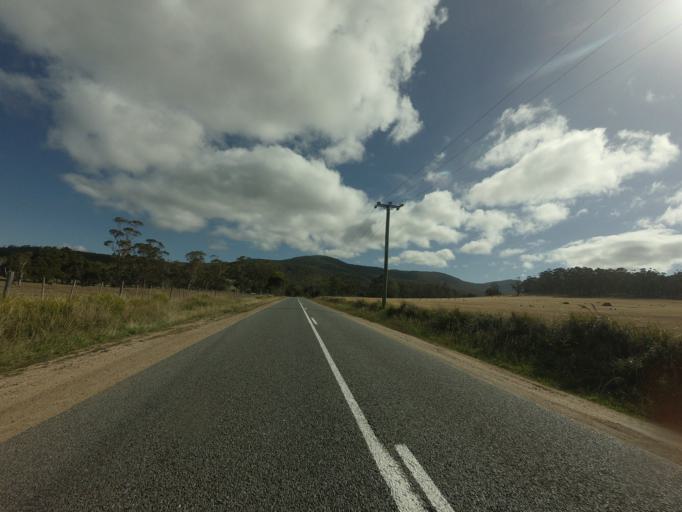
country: AU
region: Tasmania
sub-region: Break O'Day
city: St Helens
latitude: -41.7770
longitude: 148.2598
